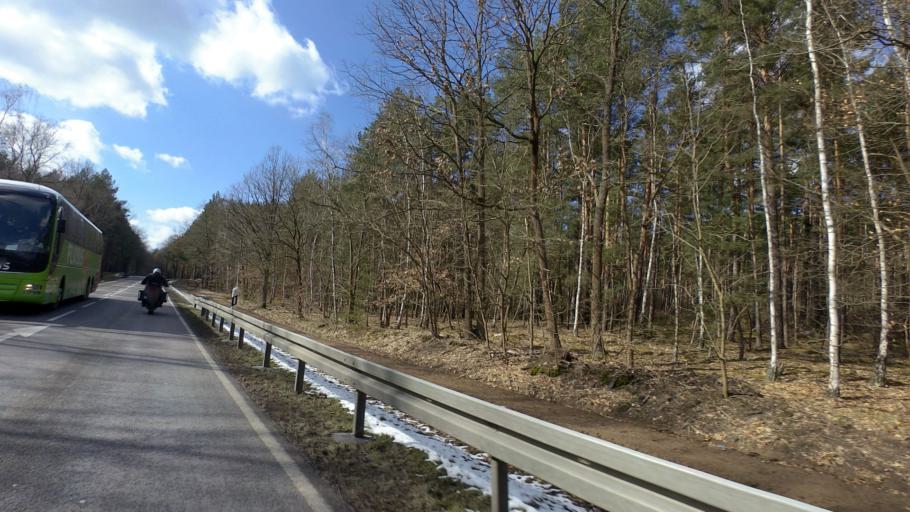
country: DE
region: Brandenburg
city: Marienwerder
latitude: 52.8575
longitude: 13.6285
